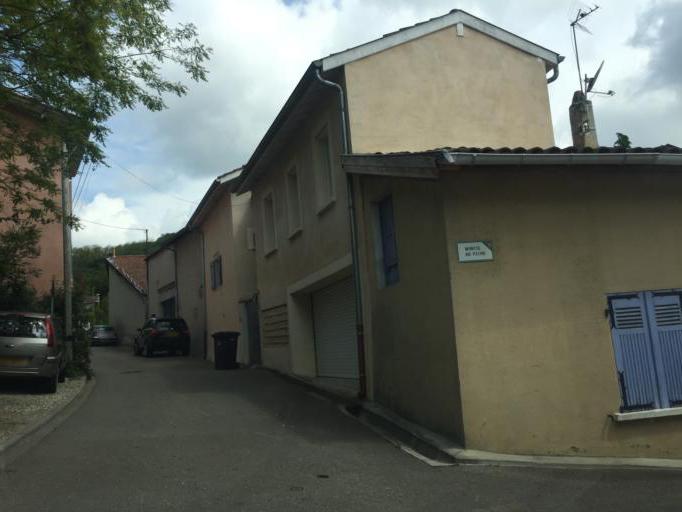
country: FR
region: Rhone-Alpes
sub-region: Departement de l'Ain
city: Beynost
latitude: 45.8422
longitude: 5.0084
